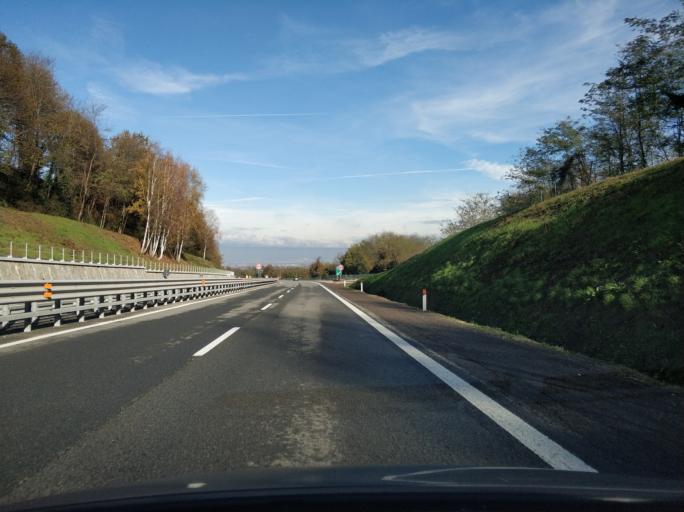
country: IT
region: Piedmont
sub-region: Provincia di Torino
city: Cuceglio
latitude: 45.3580
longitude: 7.8340
